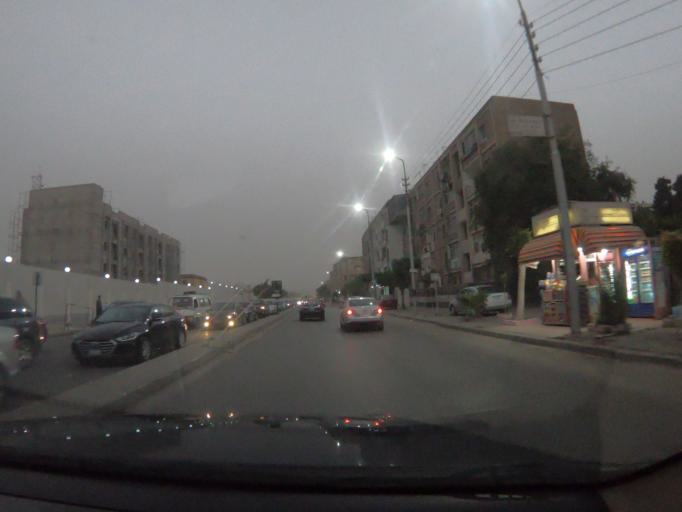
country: EG
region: Muhafazat al Qahirah
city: Cairo
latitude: 30.0848
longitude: 31.3543
